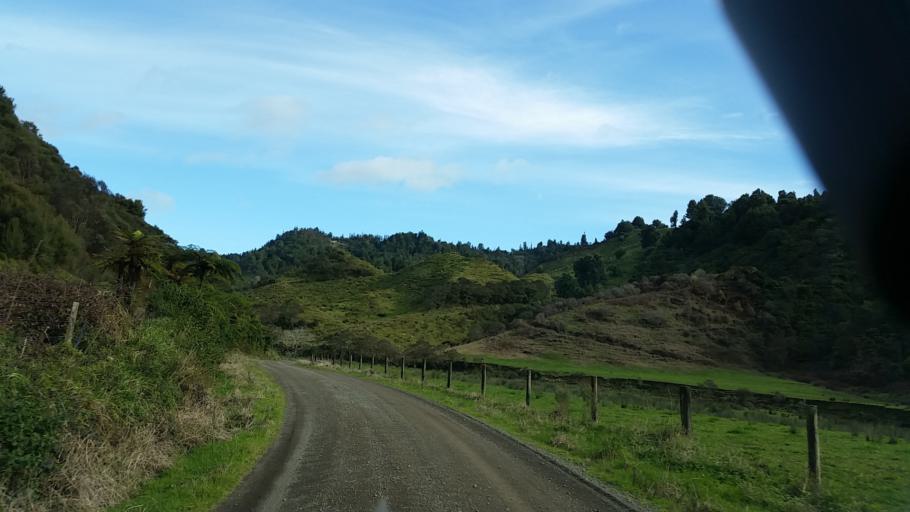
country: NZ
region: Taranaki
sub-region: New Plymouth District
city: Waitara
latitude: -39.0620
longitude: 174.4638
